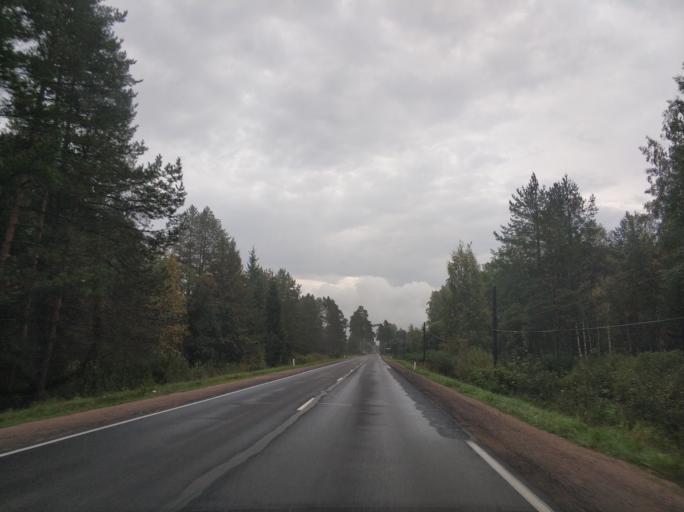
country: RU
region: Leningrad
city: Borisova Griva
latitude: 60.0872
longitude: 30.8743
